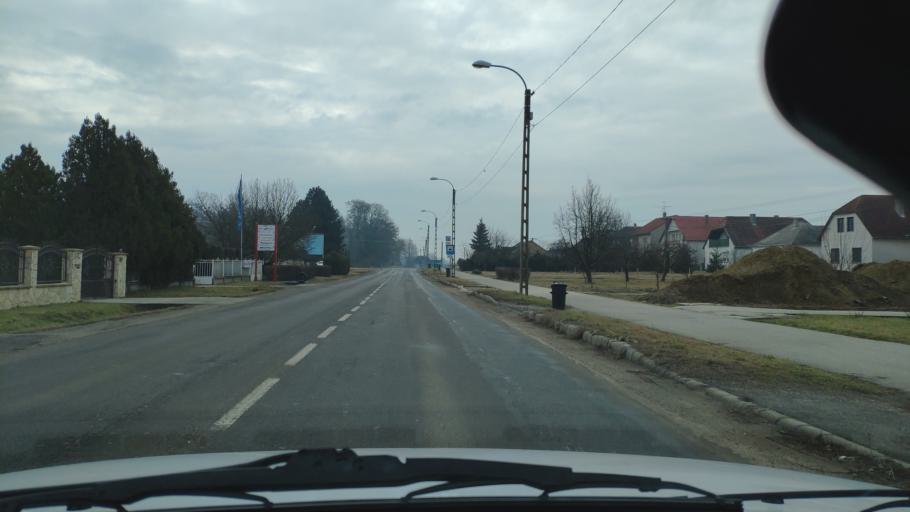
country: HU
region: Zala
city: Nagykanizsa
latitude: 46.4824
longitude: 16.9856
